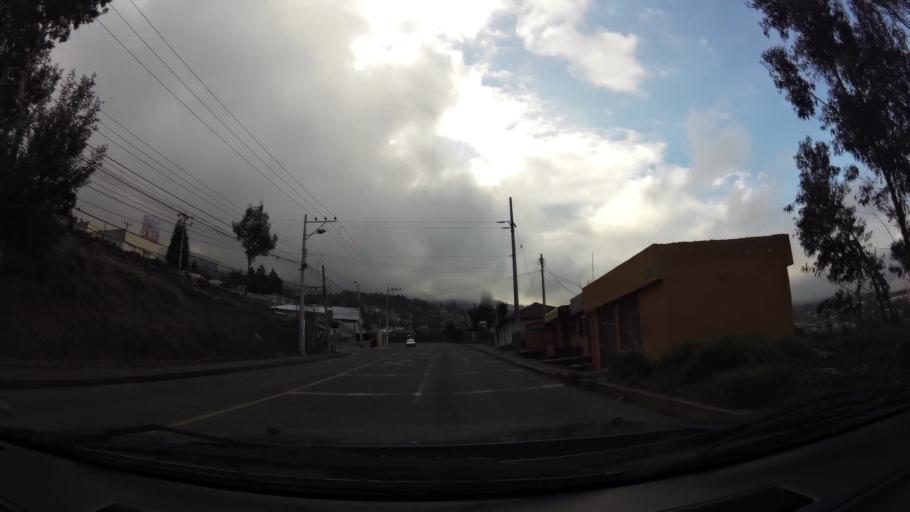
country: EC
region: Pichincha
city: Quito
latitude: -0.2804
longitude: -78.4920
